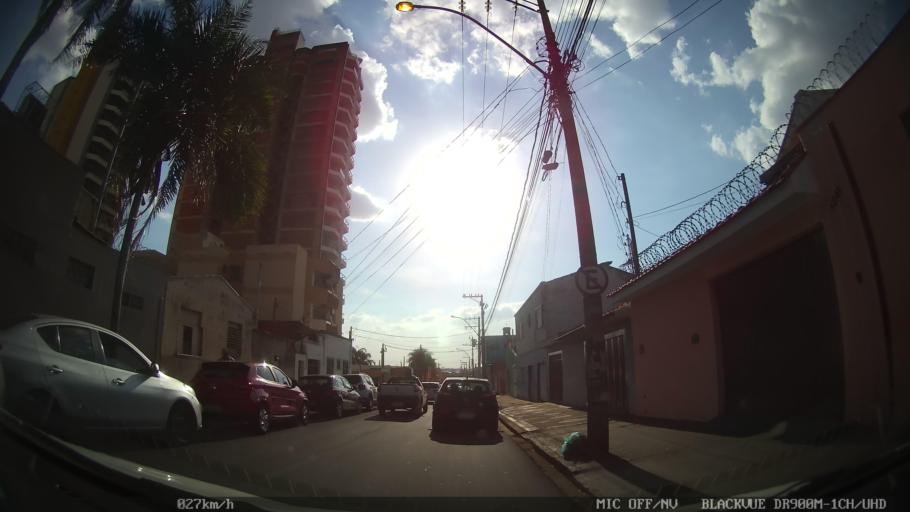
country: BR
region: Sao Paulo
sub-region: Ribeirao Preto
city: Ribeirao Preto
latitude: -21.1675
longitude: -47.8031
